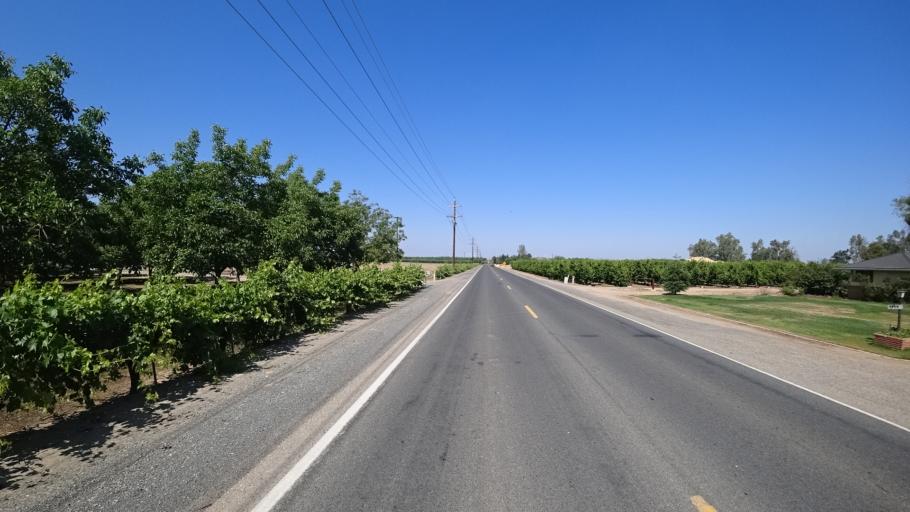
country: US
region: California
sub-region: Fresno County
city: Kingsburg
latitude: 36.4813
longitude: -119.5600
